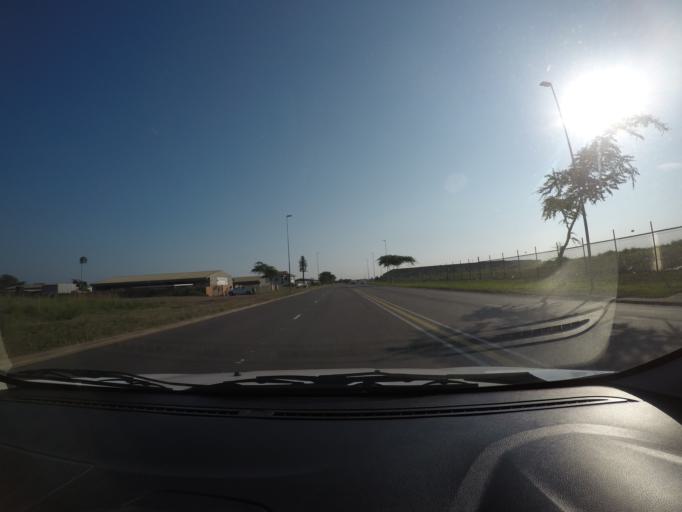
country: ZA
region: KwaZulu-Natal
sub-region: uThungulu District Municipality
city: Richards Bay
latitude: -28.7464
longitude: 32.0331
